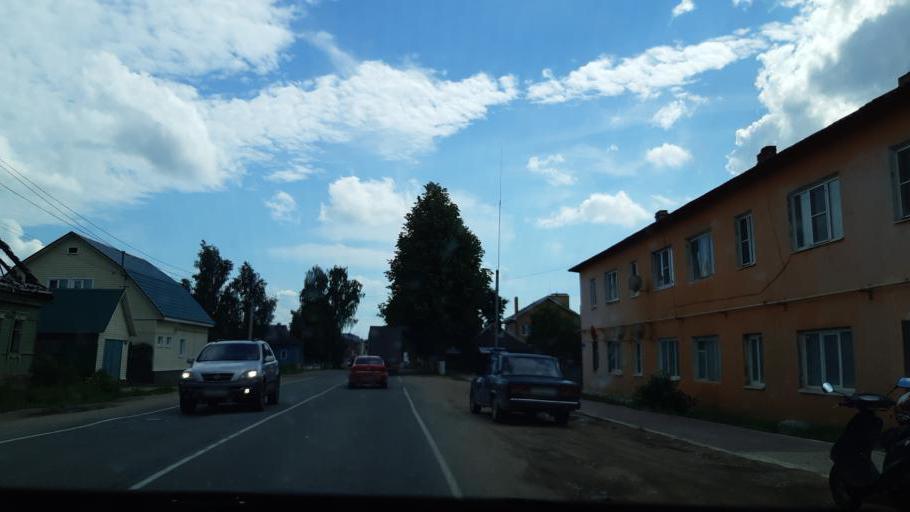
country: RU
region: Kaluga
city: Medyn'
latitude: 54.9709
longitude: 35.8585
